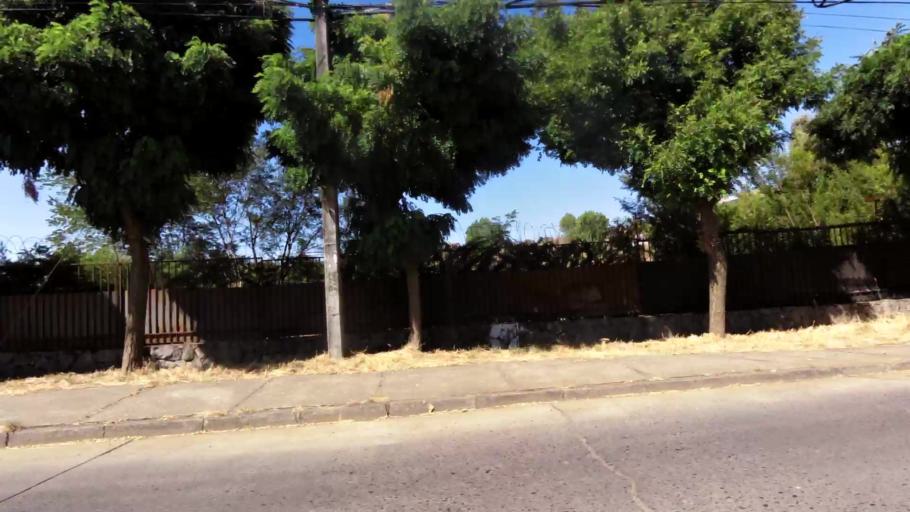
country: CL
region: Biobio
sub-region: Provincia de Concepcion
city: Concepcion
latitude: -36.7908
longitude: -73.0503
